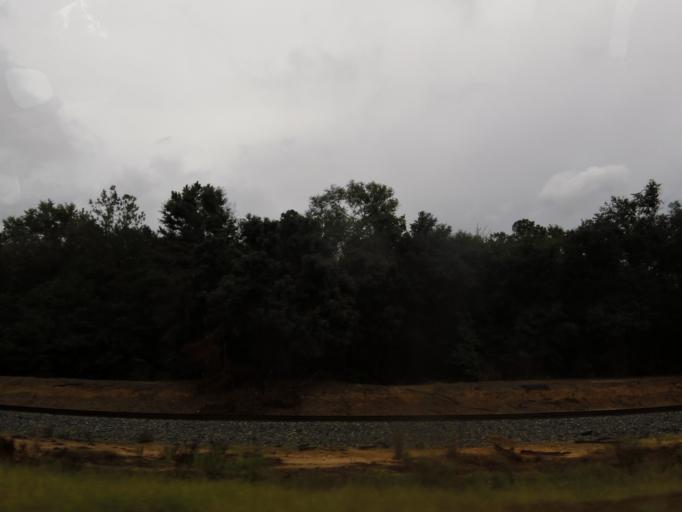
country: US
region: Georgia
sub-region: Wayne County
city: Jesup
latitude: 31.5440
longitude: -81.8051
